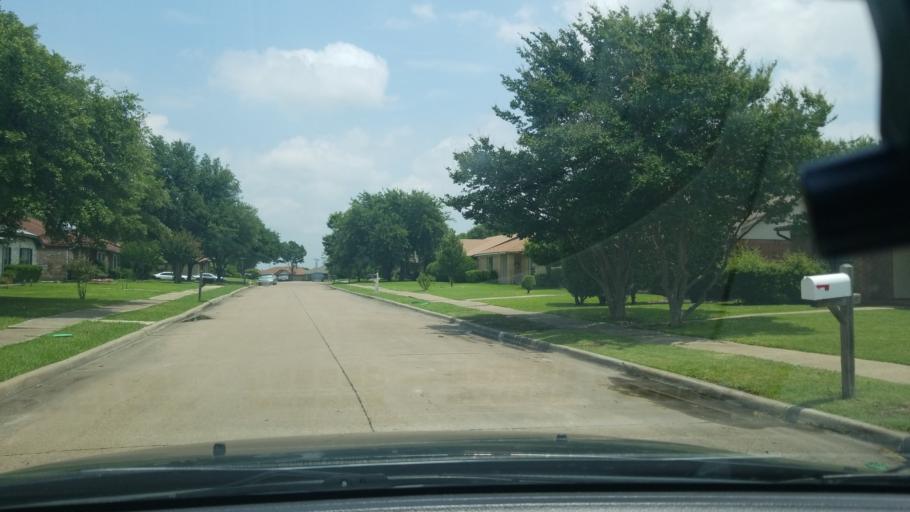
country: US
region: Texas
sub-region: Dallas County
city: Mesquite
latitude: 32.7976
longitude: -96.6143
